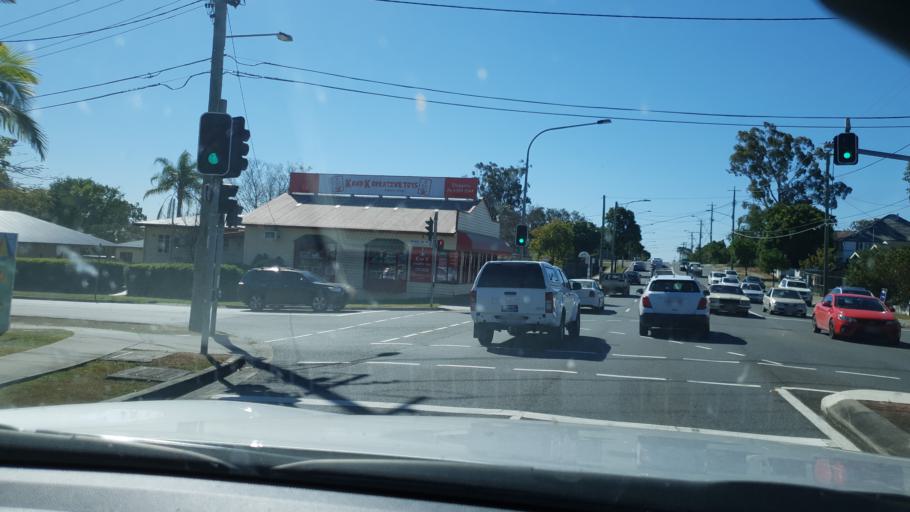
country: AU
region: Queensland
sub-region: Brisbane
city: Everton Park
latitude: -27.4295
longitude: 152.9894
